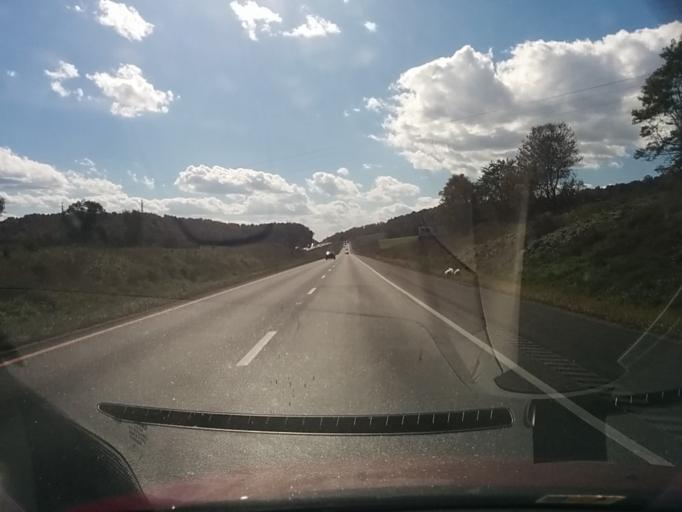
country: US
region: Virginia
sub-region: City of Buena Vista
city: Buena Vista
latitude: 37.9090
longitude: -79.2603
